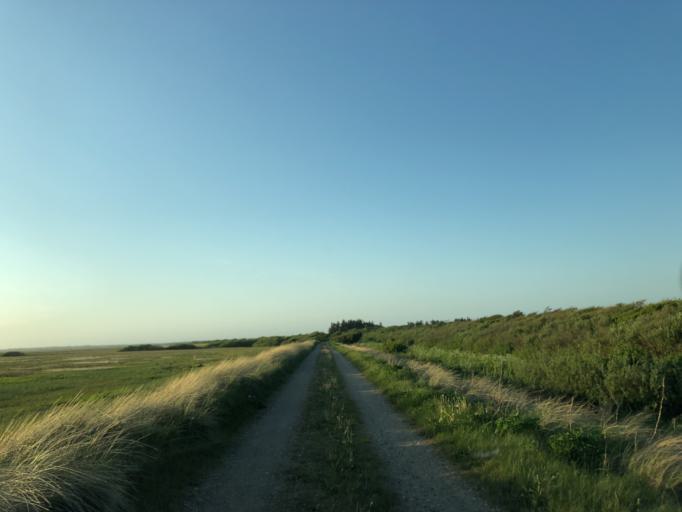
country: DK
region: Central Jutland
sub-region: Ringkobing-Skjern Kommune
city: Ringkobing
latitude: 56.2252
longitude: 8.1668
